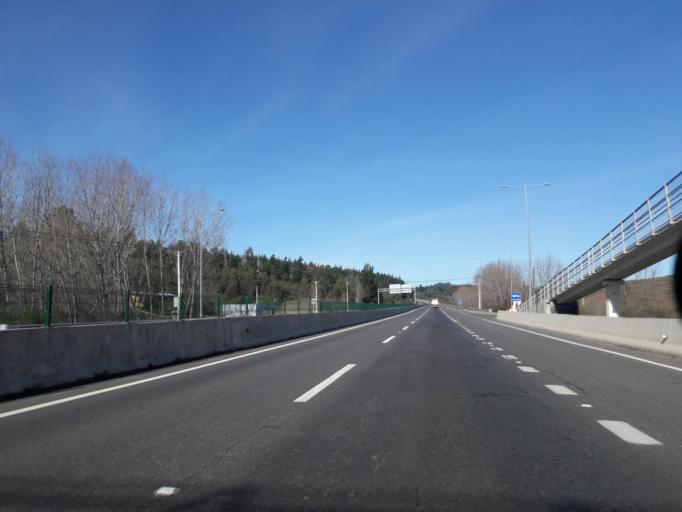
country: CL
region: Biobio
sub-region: Provincia de Concepcion
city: Chiguayante
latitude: -36.9168
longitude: -72.7753
